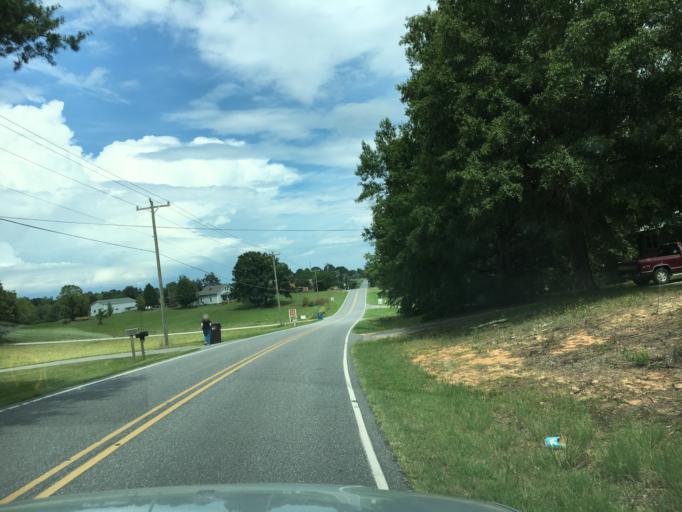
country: US
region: North Carolina
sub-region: Catawba County
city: Maiden
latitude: 35.6052
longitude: -81.1805
